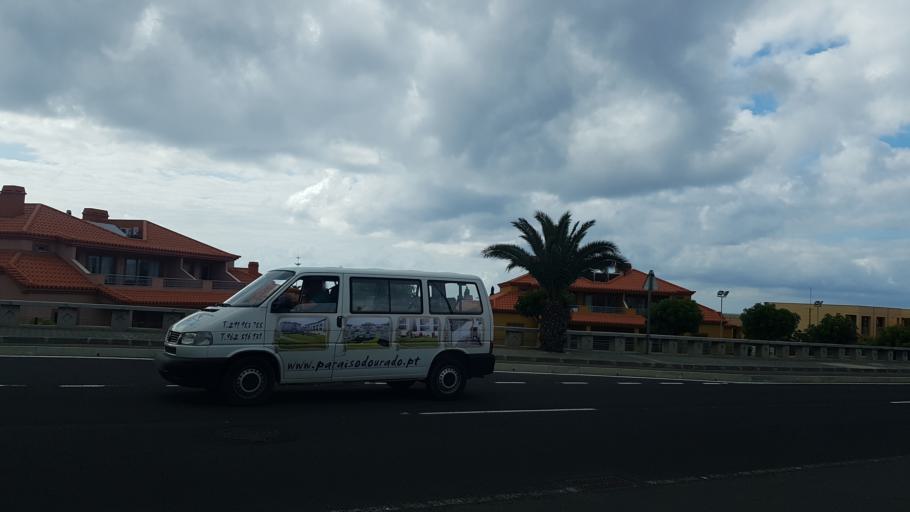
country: PT
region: Madeira
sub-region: Porto Santo
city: Vila de Porto Santo
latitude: 33.0437
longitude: -16.3583
